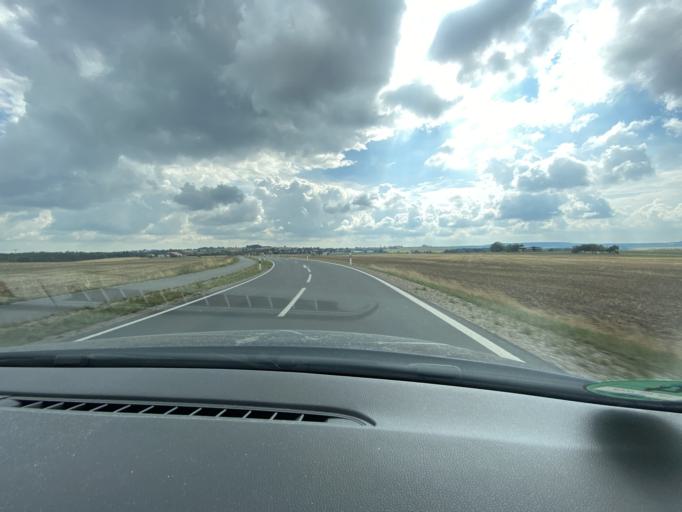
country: DE
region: Saxony
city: Tharandt
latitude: 51.0155
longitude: 13.5867
